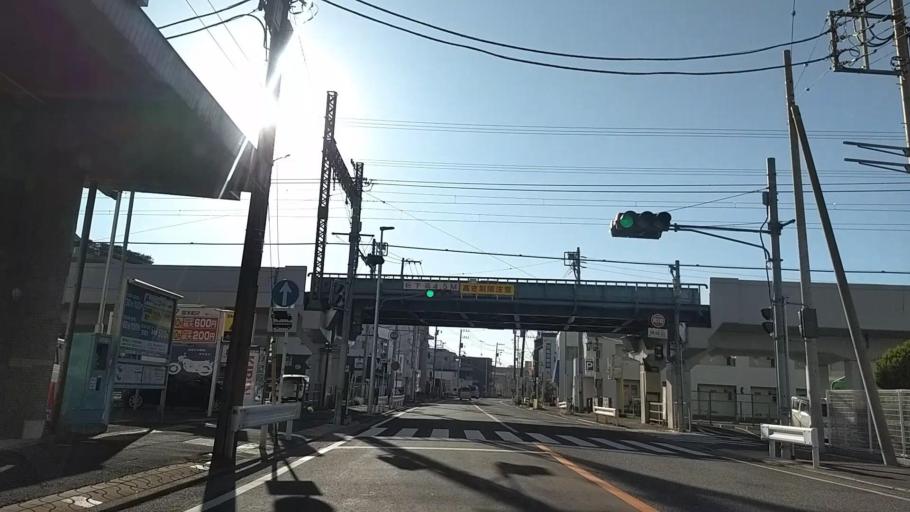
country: JP
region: Kanagawa
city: Atsugi
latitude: 35.4418
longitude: 139.3702
